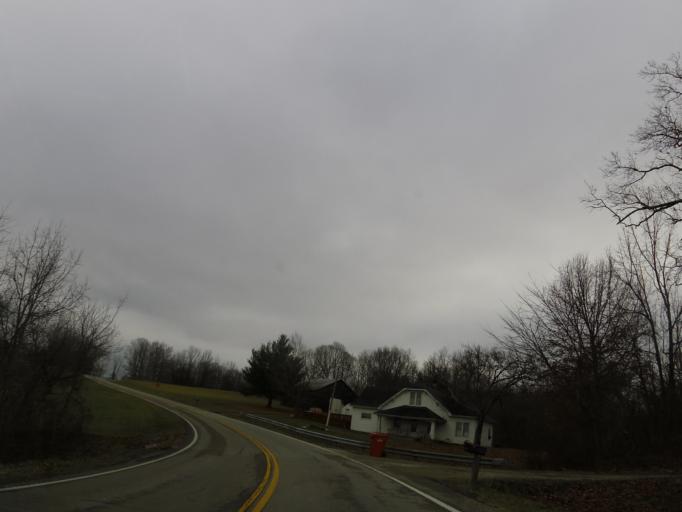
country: US
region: Kentucky
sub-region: Franklin County
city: Frankfort
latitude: 38.3400
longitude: -84.9632
